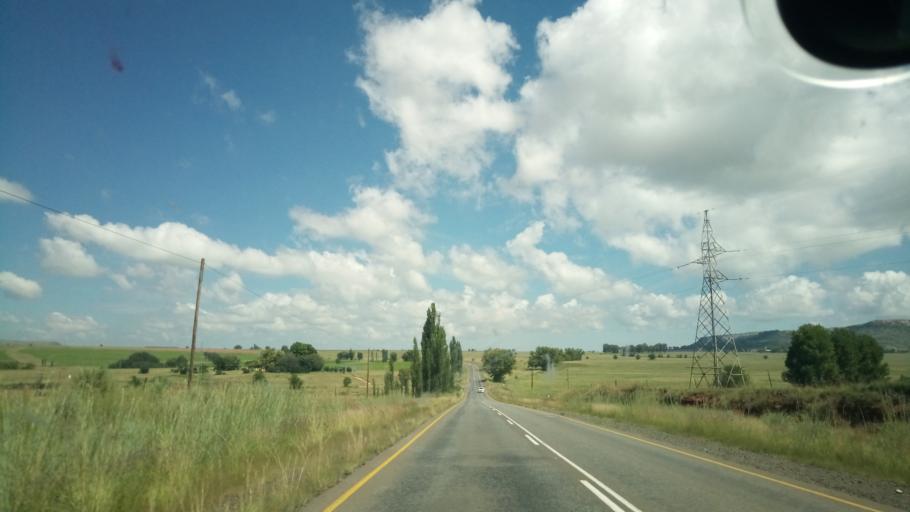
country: ZA
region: Orange Free State
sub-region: Thabo Mofutsanyana District Municipality
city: Ficksburg
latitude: -28.8927
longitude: 27.7634
